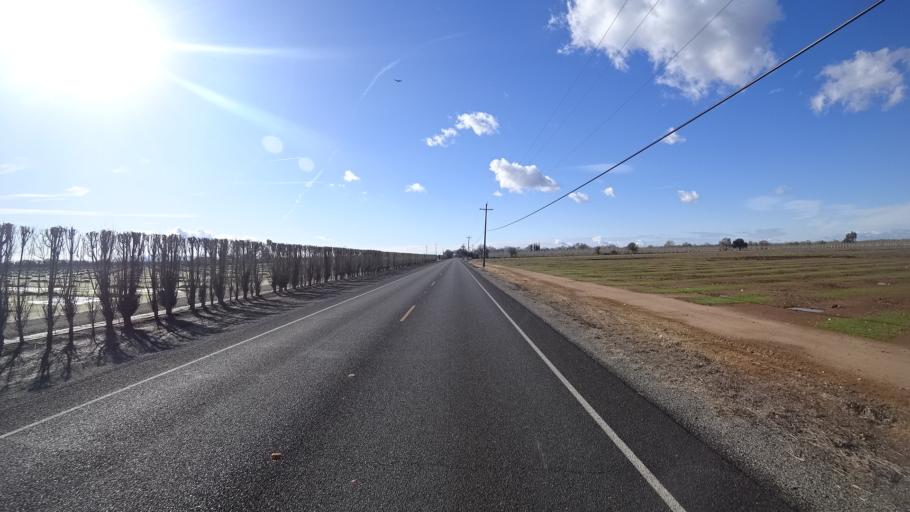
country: US
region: California
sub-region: Butte County
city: Gridley
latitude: 39.3645
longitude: -121.6147
